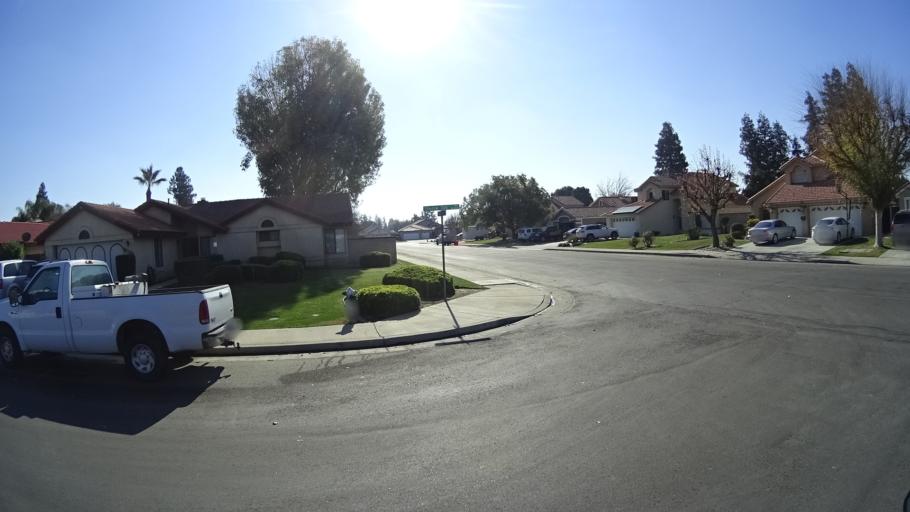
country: US
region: California
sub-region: Kern County
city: Greenacres
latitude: 35.3223
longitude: -119.1150
